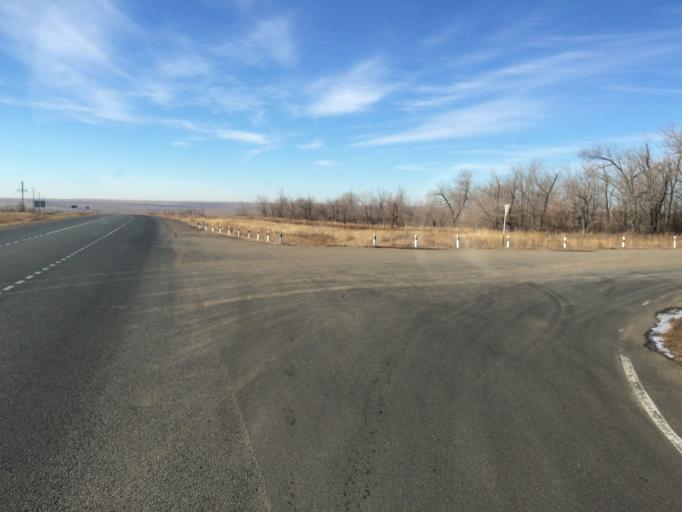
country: KZ
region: Aqtoebe
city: Aqtobe
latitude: 50.2476
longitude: 56.7894
